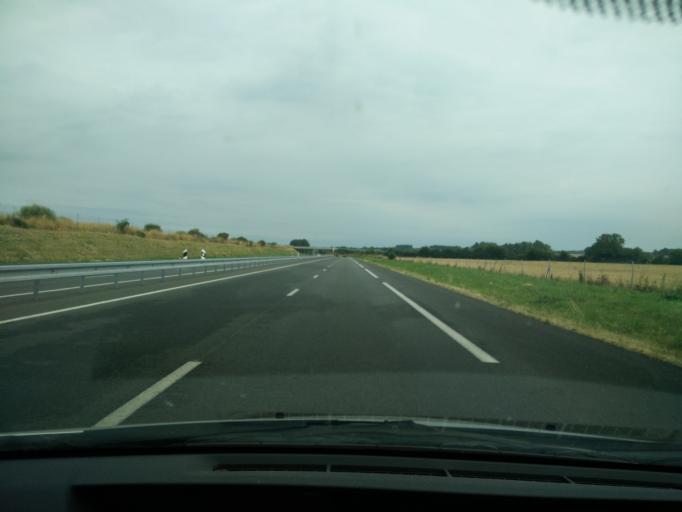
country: FR
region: Pays de la Loire
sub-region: Departement de Maine-et-Loire
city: Saint-Jean
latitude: 47.2684
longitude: -0.3356
